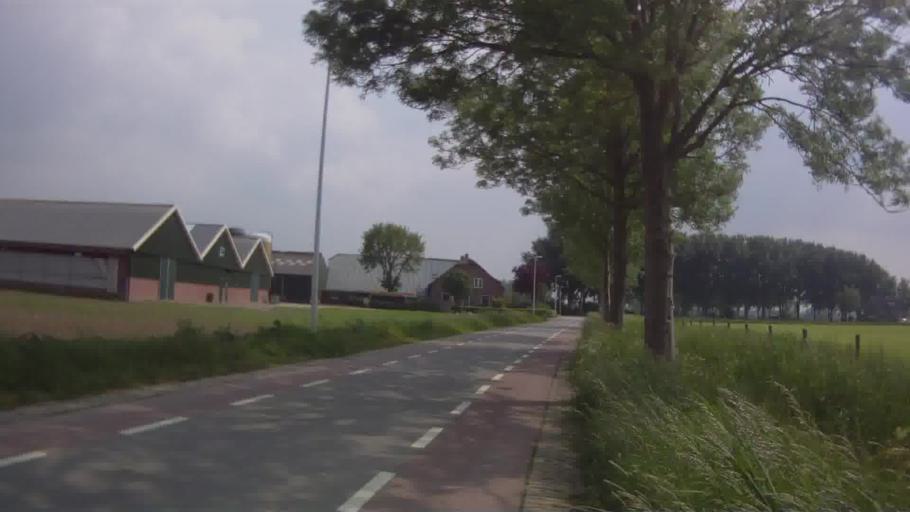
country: NL
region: Utrecht
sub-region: Gemeente Bunnik
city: Bunnik
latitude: 52.0574
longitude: 5.1897
